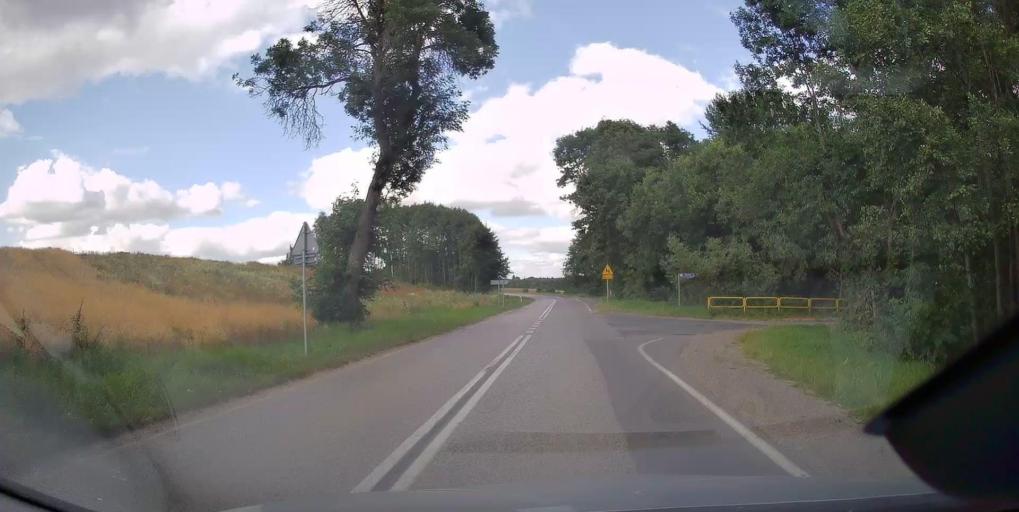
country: PL
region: Swietokrzyskie
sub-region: Powiat kielecki
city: Nowa Slupia
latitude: 50.8363
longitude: 21.0901
